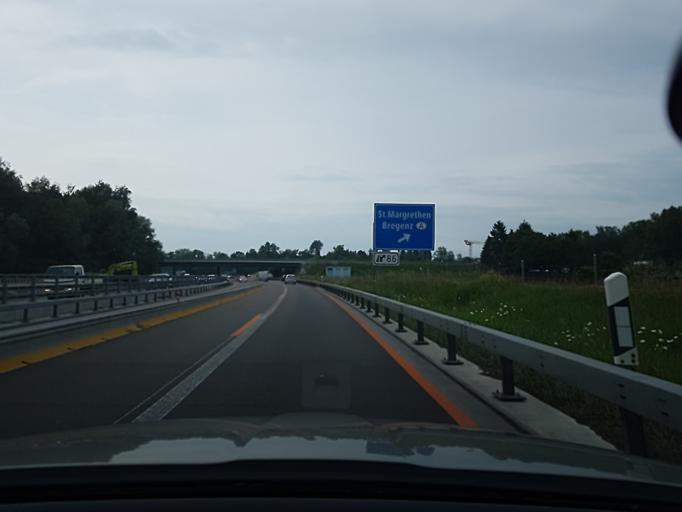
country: AT
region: Vorarlberg
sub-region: Politischer Bezirk Bregenz
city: Hochst
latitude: 47.4517
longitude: 9.6531
